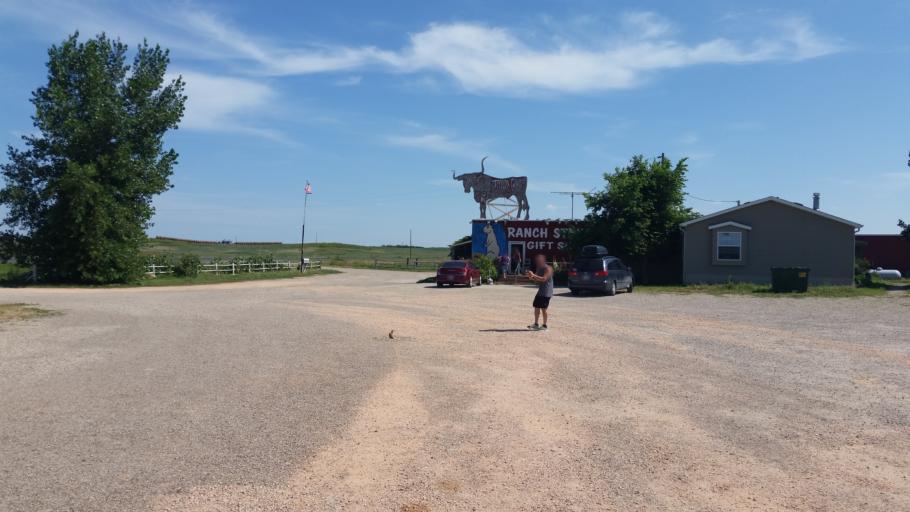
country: US
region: South Dakota
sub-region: Haakon County
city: Philip
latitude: 43.8399
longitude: -101.8760
